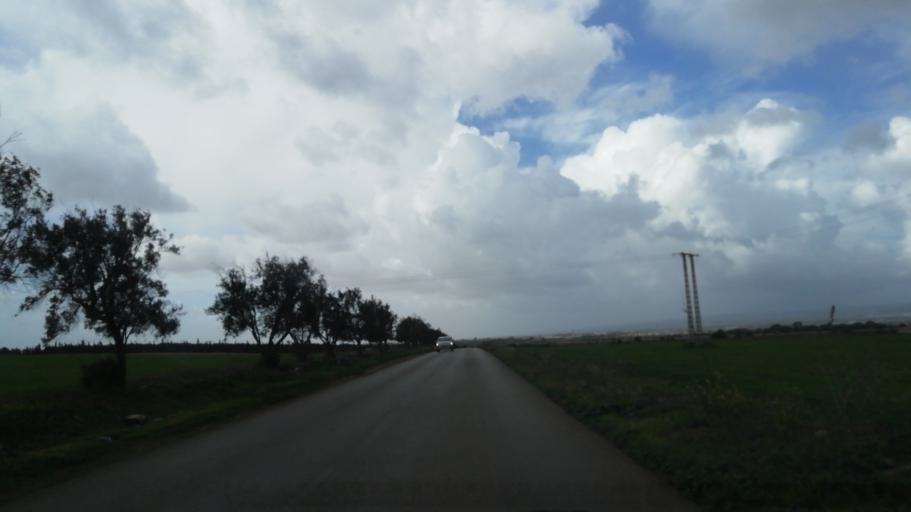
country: DZ
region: Oran
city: Sidi ech Chahmi
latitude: 35.6256
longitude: -0.5384
